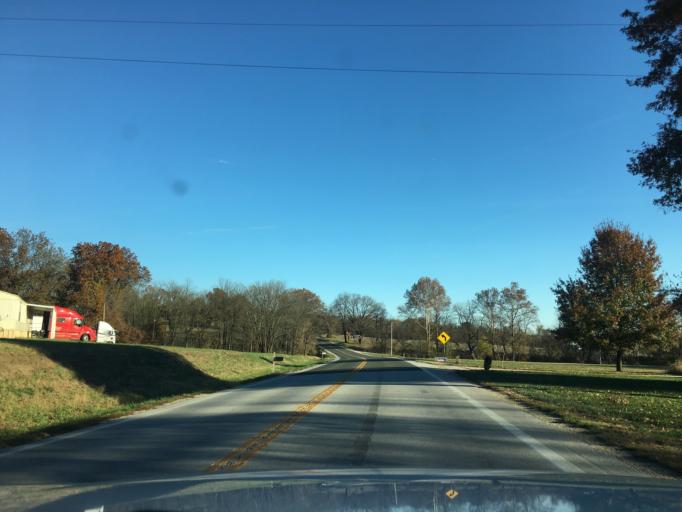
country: US
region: Missouri
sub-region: Franklin County
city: New Haven
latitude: 38.5998
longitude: -91.2557
